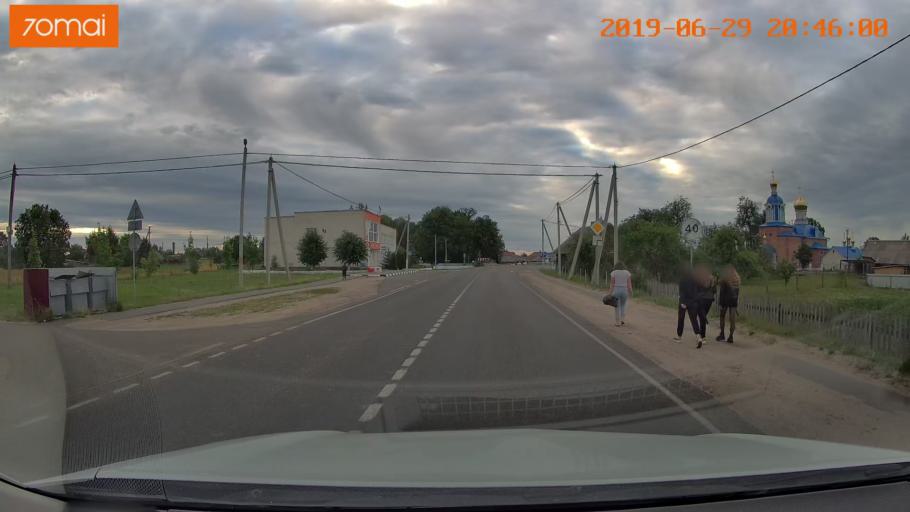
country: BY
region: Brest
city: Hantsavichy
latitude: 52.6282
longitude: 26.3076
